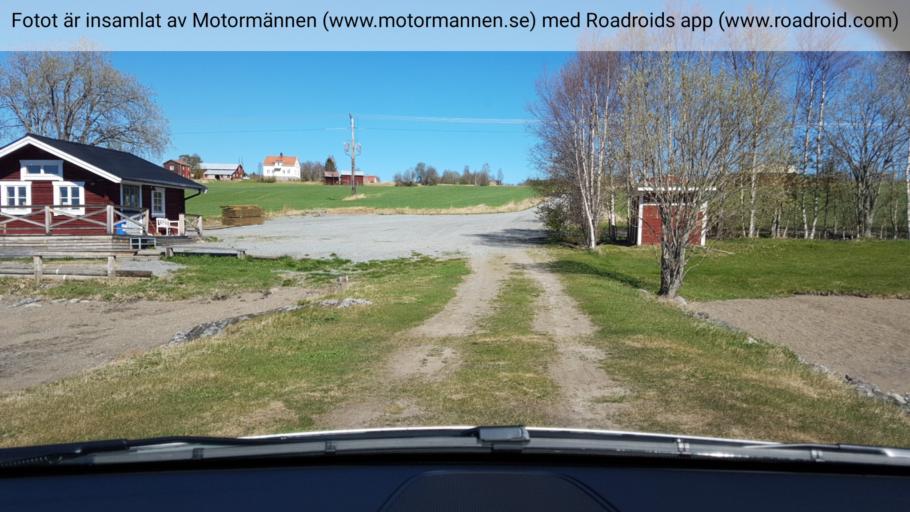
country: SE
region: Jaemtland
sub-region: Bergs Kommun
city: Hoverberg
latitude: 63.0408
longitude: 14.4489
